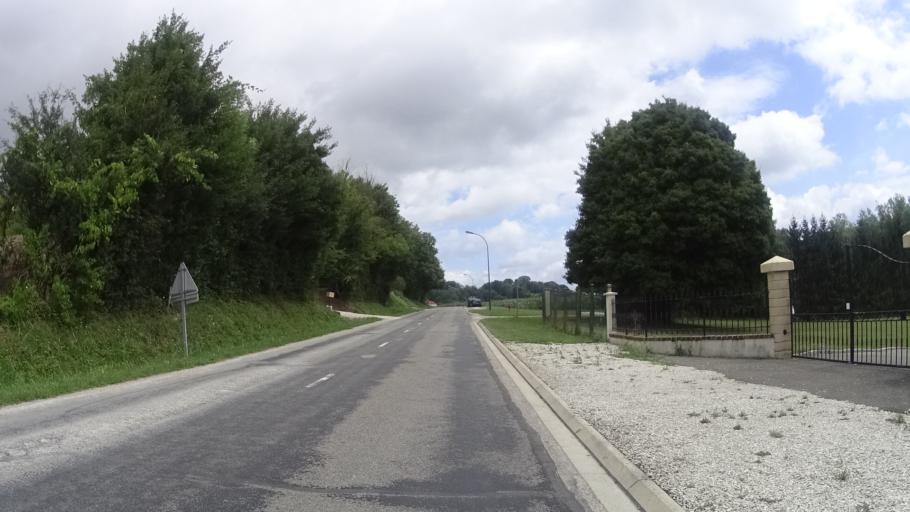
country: FR
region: Champagne-Ardenne
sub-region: Departement de l'Aube
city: Bouilly
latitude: 48.1181
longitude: 3.9835
